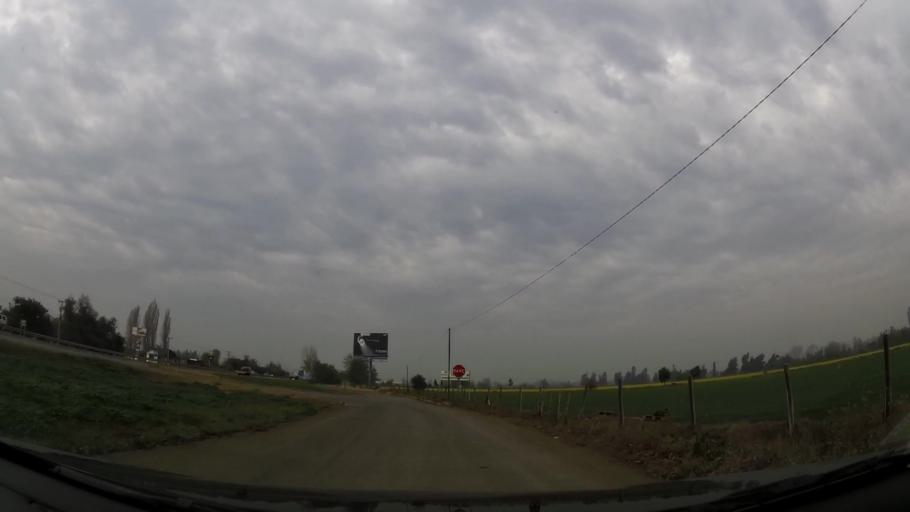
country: CL
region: Santiago Metropolitan
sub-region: Provincia de Chacabuco
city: Chicureo Abajo
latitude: -33.2283
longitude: -70.7625
